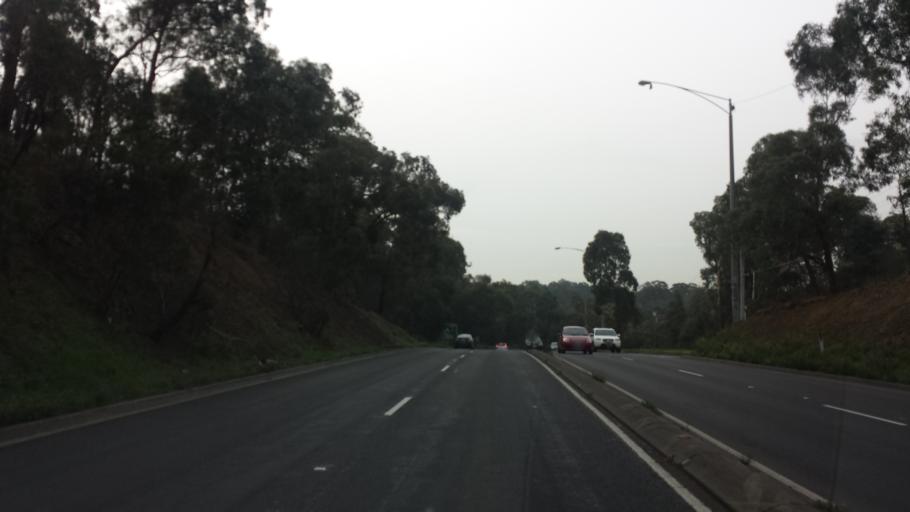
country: AU
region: Victoria
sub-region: Nillumbik
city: Eltham
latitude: -37.7362
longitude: 145.1345
